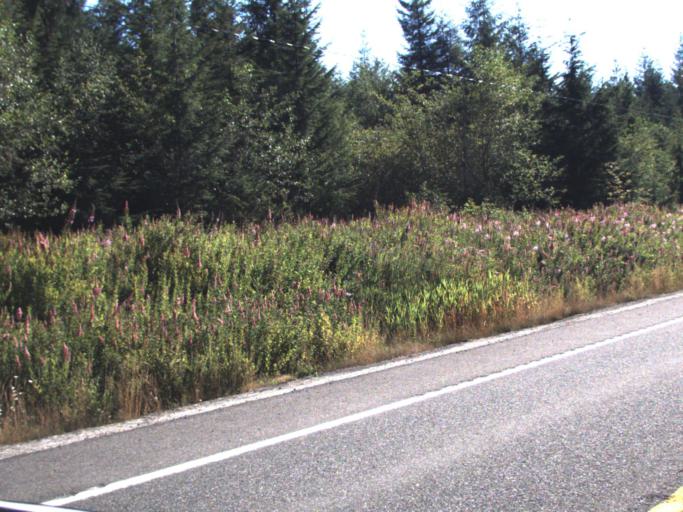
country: US
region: Washington
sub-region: King County
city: Enumclaw
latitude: 47.1636
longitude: -121.8960
